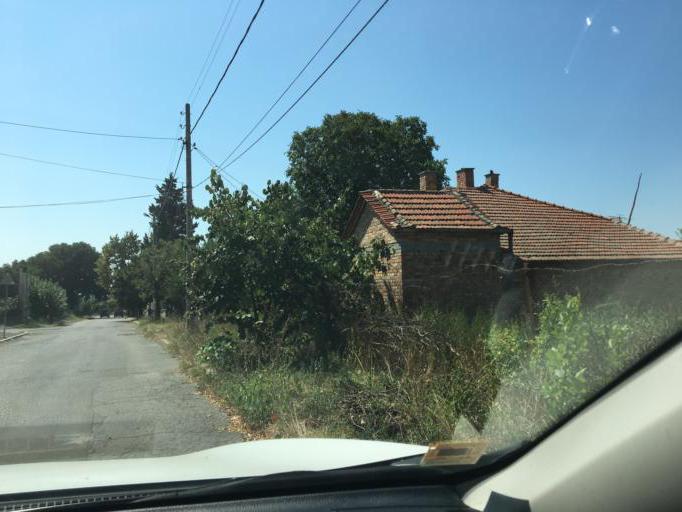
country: BG
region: Burgas
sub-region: Obshtina Kameno
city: Kameno
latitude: 42.6288
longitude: 27.3920
